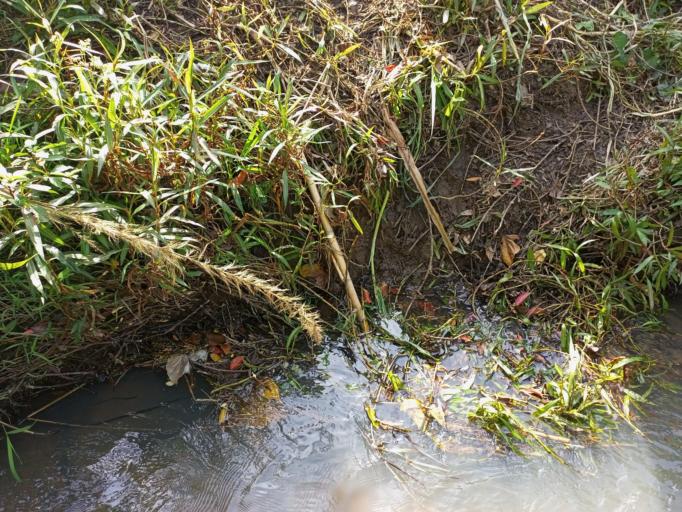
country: CD
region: Eastern Province
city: Bunia
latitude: 1.5372
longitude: 30.2954
